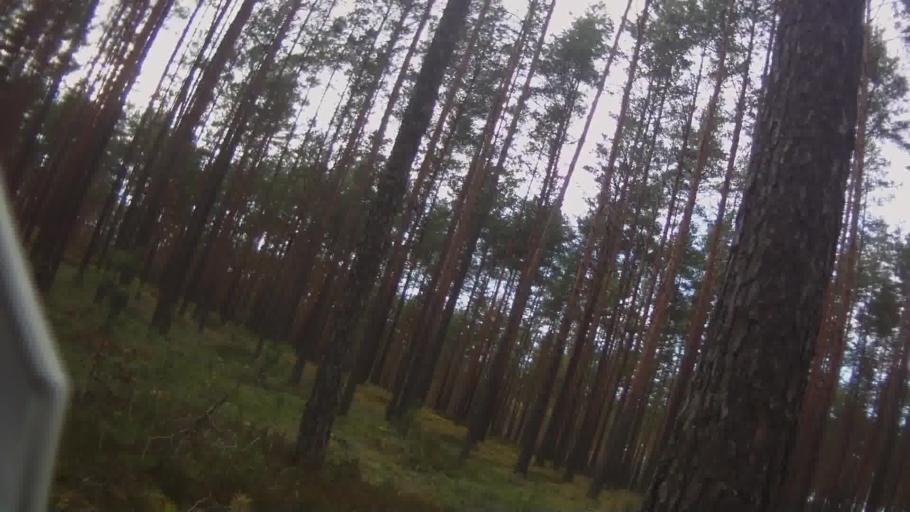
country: LV
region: Riga
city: Jaunciems
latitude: 57.0688
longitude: 24.1790
